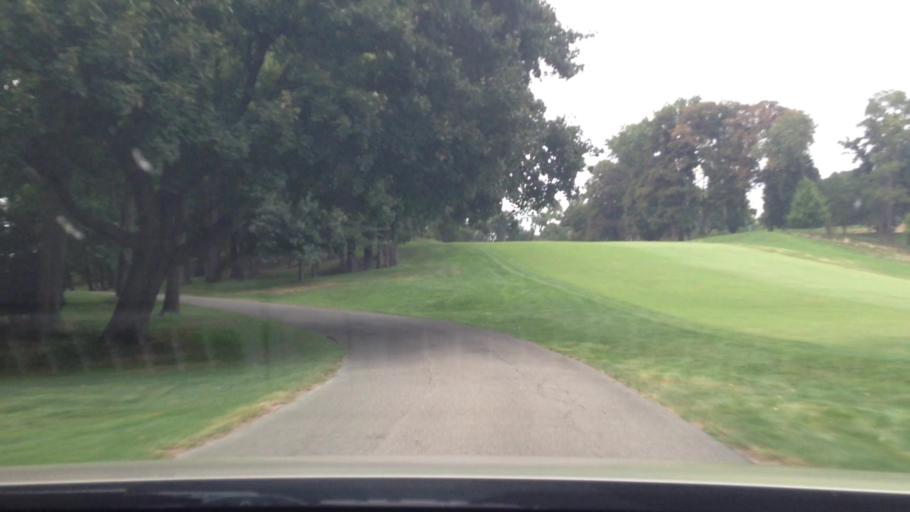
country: US
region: New York
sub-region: Nassau County
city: Manhasset Hills
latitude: 40.7683
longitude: -73.6962
